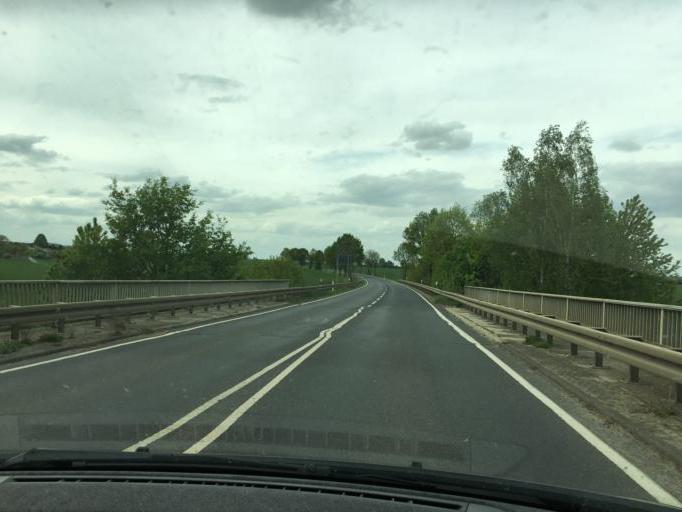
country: DE
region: North Rhine-Westphalia
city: Zulpich
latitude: 50.7293
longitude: 6.6719
